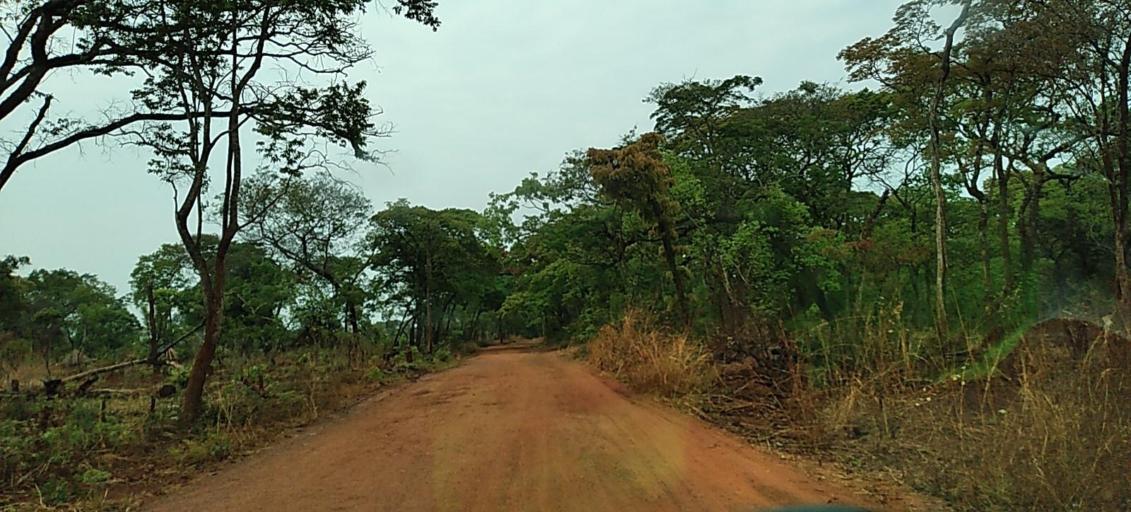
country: ZM
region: North-Western
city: Solwezi
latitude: -12.3119
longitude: 26.5222
